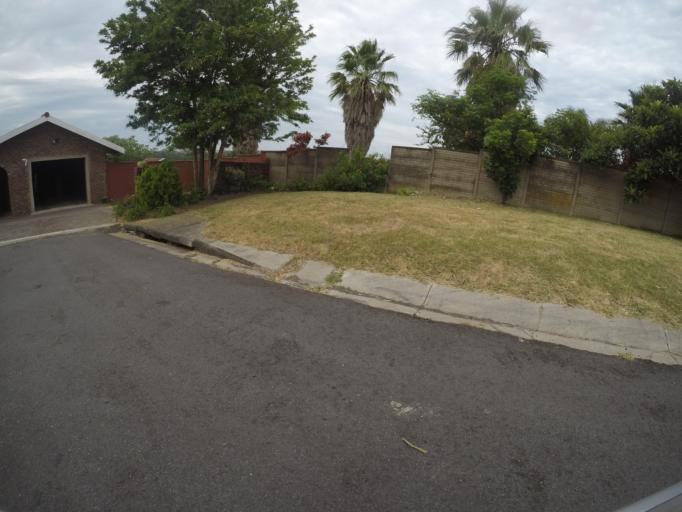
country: ZA
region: Eastern Cape
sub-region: Buffalo City Metropolitan Municipality
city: East London
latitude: -32.9997
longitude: 27.8790
